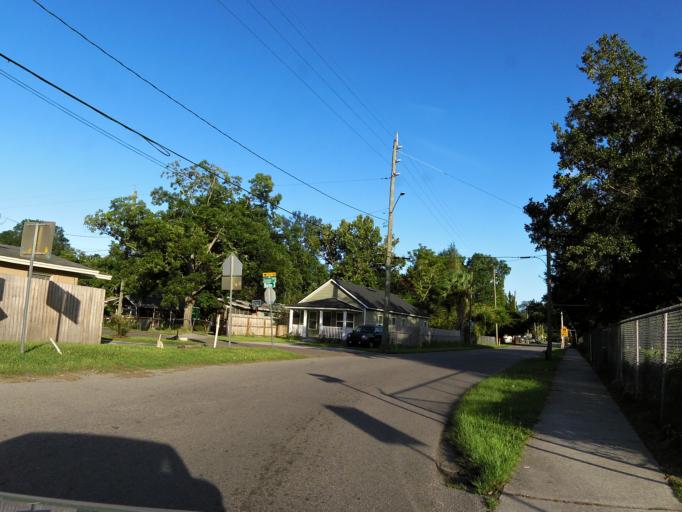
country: US
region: Florida
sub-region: Duval County
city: Jacksonville
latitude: 30.3404
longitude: -81.6896
